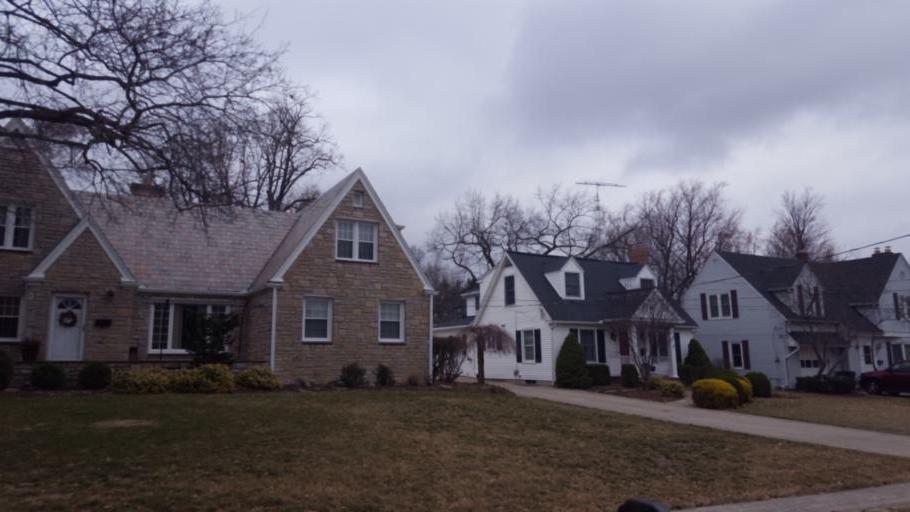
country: US
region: Ohio
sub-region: Richland County
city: Shelby
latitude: 40.8761
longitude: -82.6510
